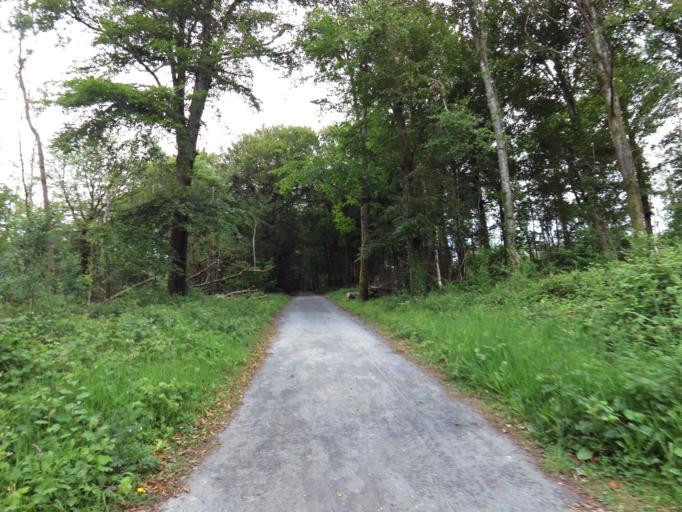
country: IE
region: Connaught
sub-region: County Galway
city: Gort
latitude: 53.0794
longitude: -8.8488
